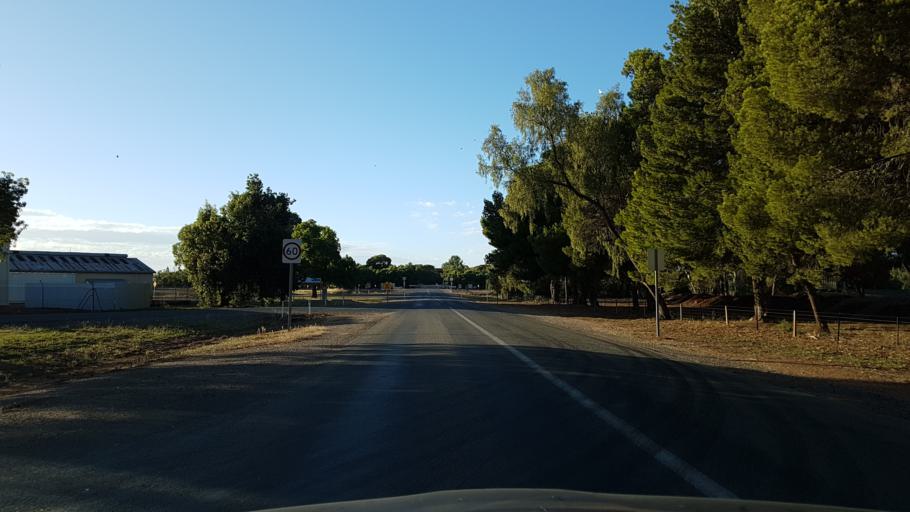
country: AU
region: South Australia
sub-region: Port Pirie City and Dists
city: Crystal Brook
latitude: -33.2747
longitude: 138.3554
